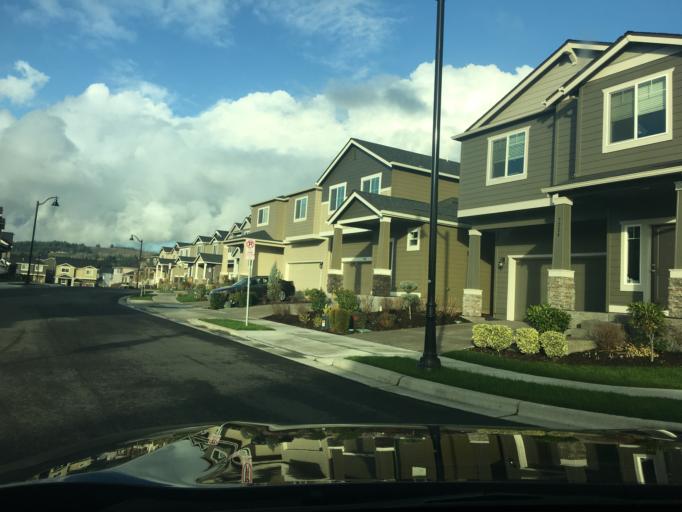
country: US
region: Oregon
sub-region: Washington County
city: Bethany
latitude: 45.5719
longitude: -122.8503
